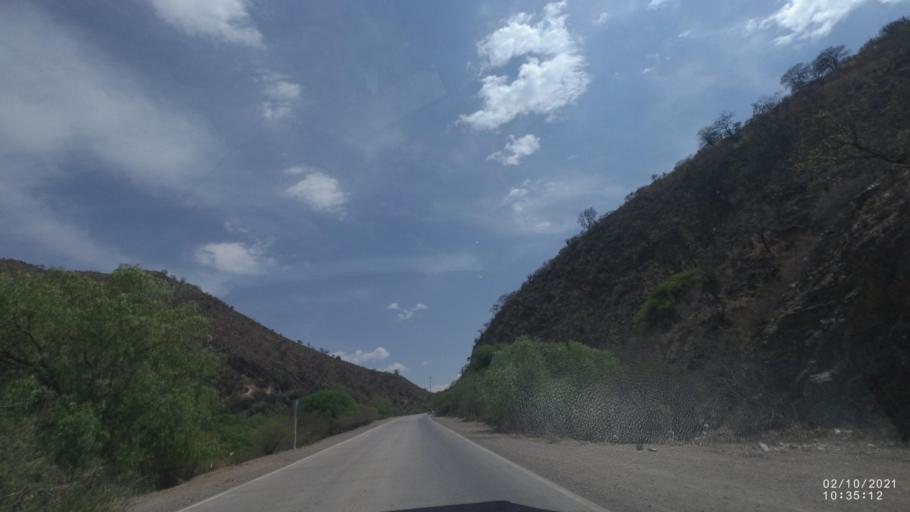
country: BO
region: Cochabamba
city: Capinota
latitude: -17.6643
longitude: -66.2577
